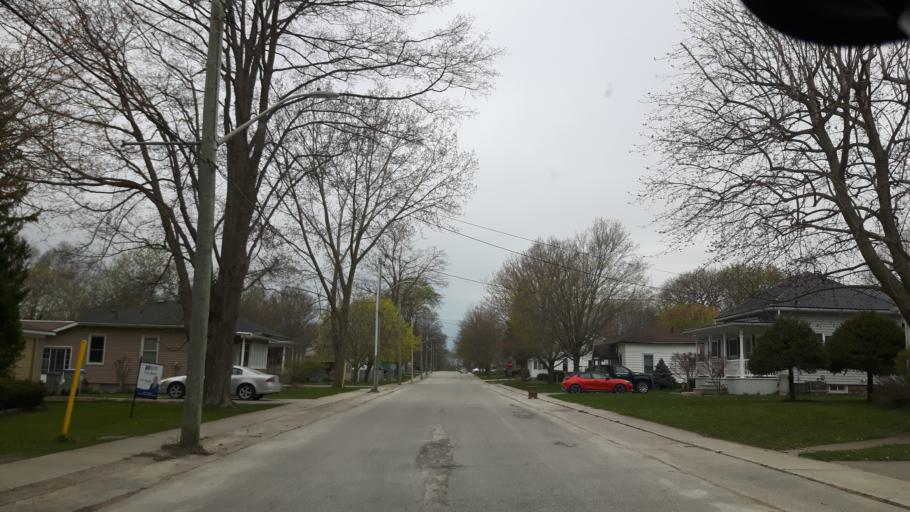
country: CA
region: Ontario
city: Bluewater
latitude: 43.6195
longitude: -81.5427
